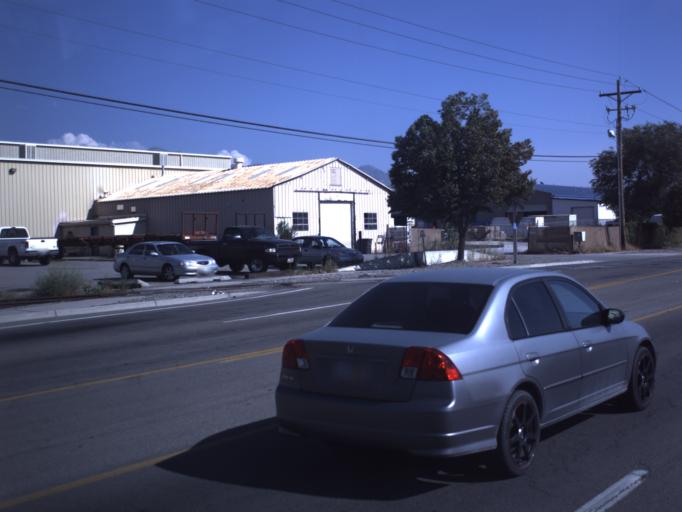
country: US
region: Utah
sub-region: Utah County
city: Lindon
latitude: 40.3373
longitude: -111.7394
